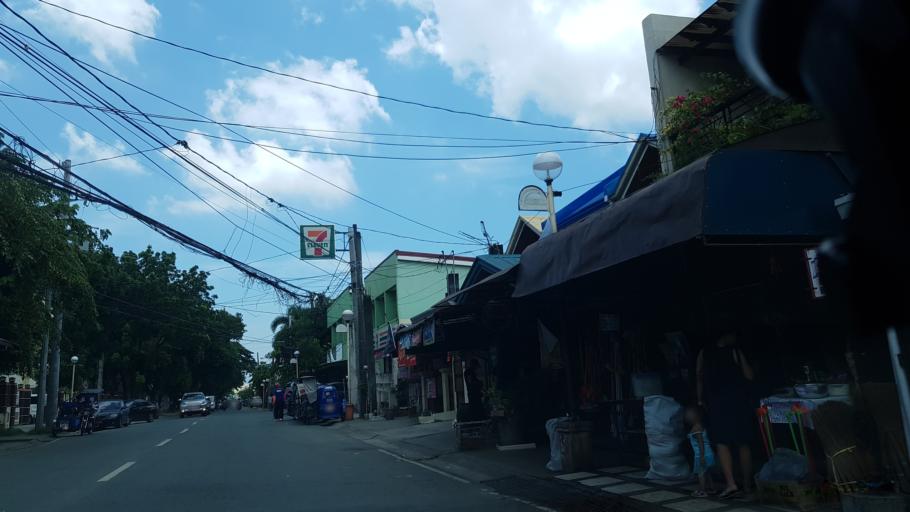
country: PH
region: Calabarzon
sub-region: Province of Rizal
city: Las Pinas
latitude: 14.4324
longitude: 120.9860
